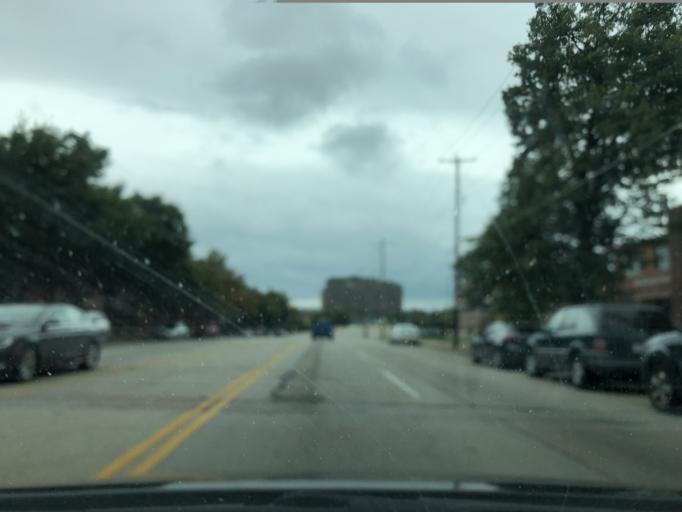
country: US
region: Kentucky
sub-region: Kenton County
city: Ludlow
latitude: 39.1075
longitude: -84.5280
